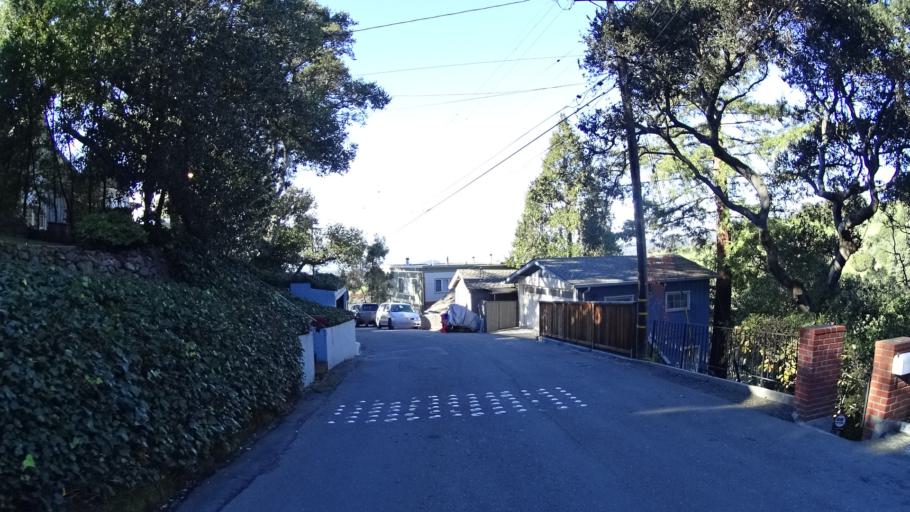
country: US
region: California
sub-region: Alameda County
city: Piedmont
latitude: 37.8304
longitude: -122.2301
